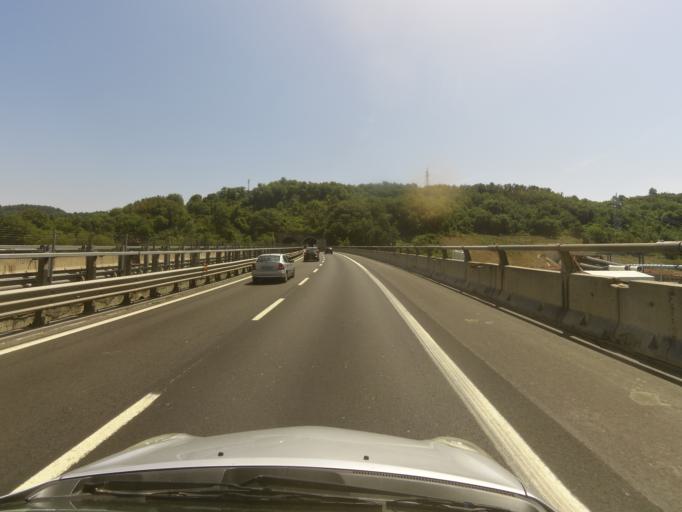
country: IT
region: Tuscany
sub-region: Province of Florence
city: Cavallina
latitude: 43.9554
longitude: 11.2095
